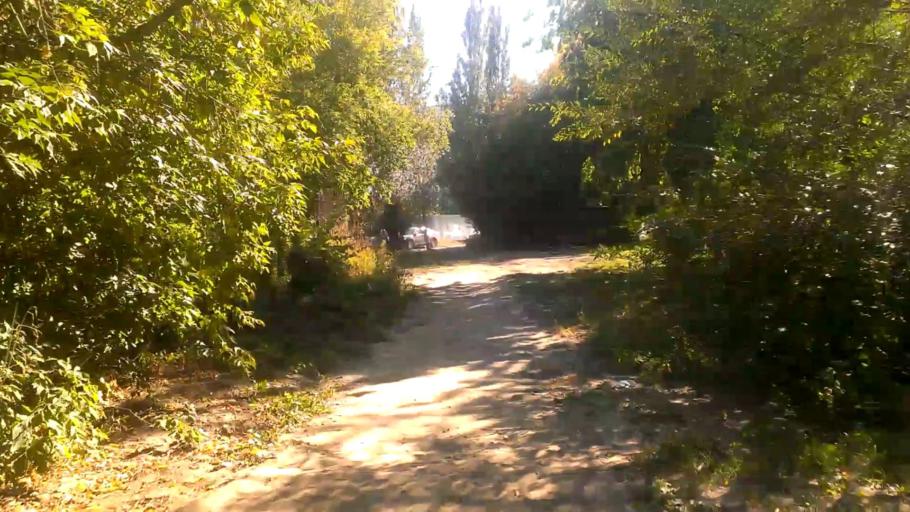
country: RU
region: Altai Krai
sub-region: Gorod Barnaulskiy
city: Barnaul
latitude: 53.3725
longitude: 83.6851
